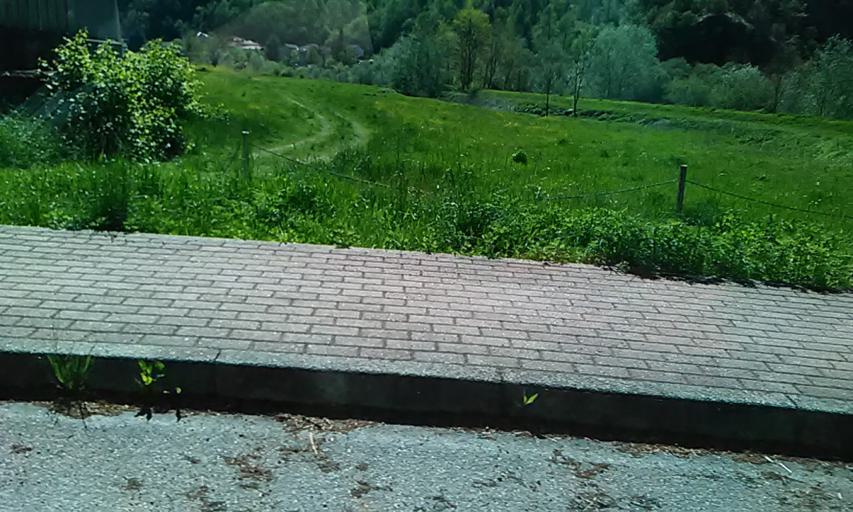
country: IT
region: Piedmont
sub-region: Provincia di Biella
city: Pray
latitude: 45.6746
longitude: 8.2147
